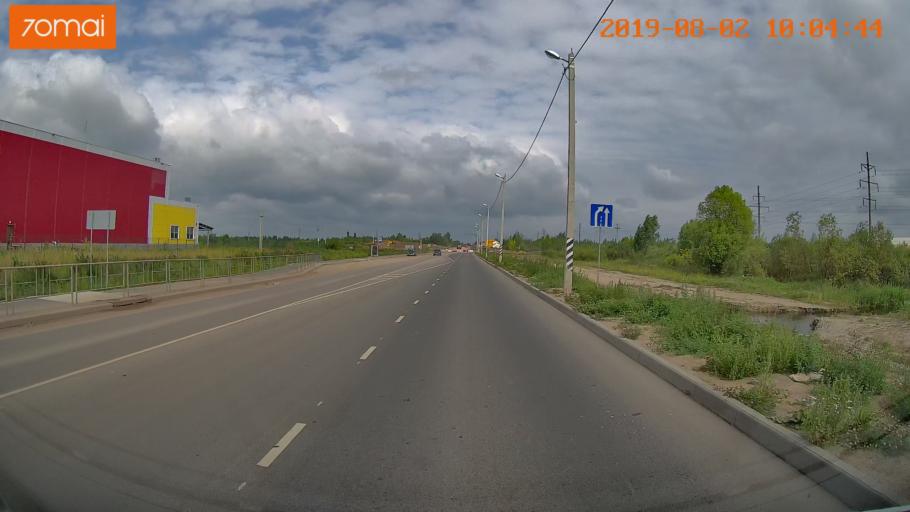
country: RU
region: Ivanovo
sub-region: Gorod Ivanovo
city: Ivanovo
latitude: 56.9749
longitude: 40.9231
